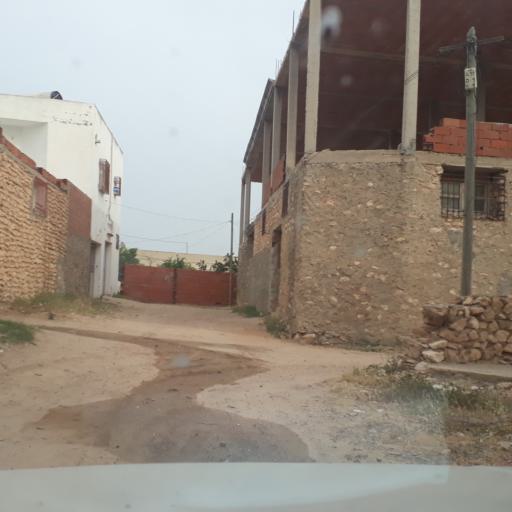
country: TN
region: Safaqis
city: Al Qarmadah
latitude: 34.8258
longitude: 10.7759
